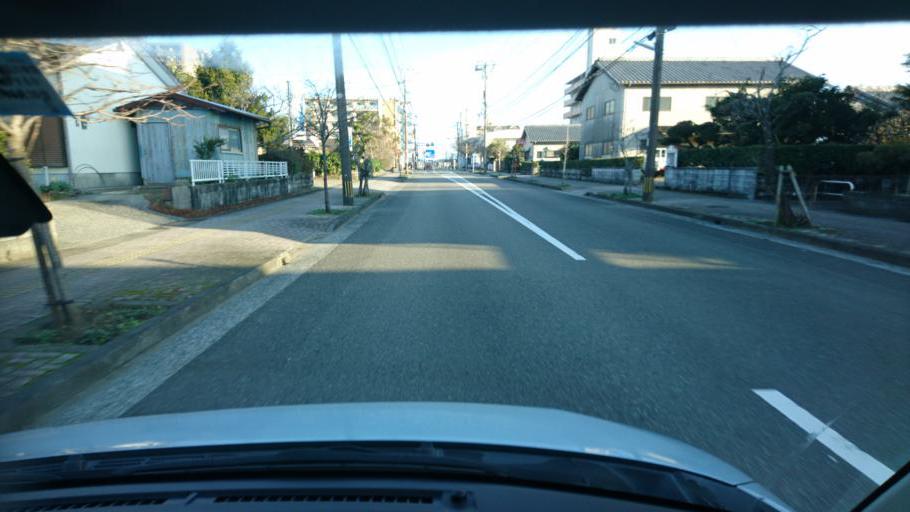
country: JP
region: Miyazaki
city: Miyazaki-shi
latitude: 31.8288
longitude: 131.4199
